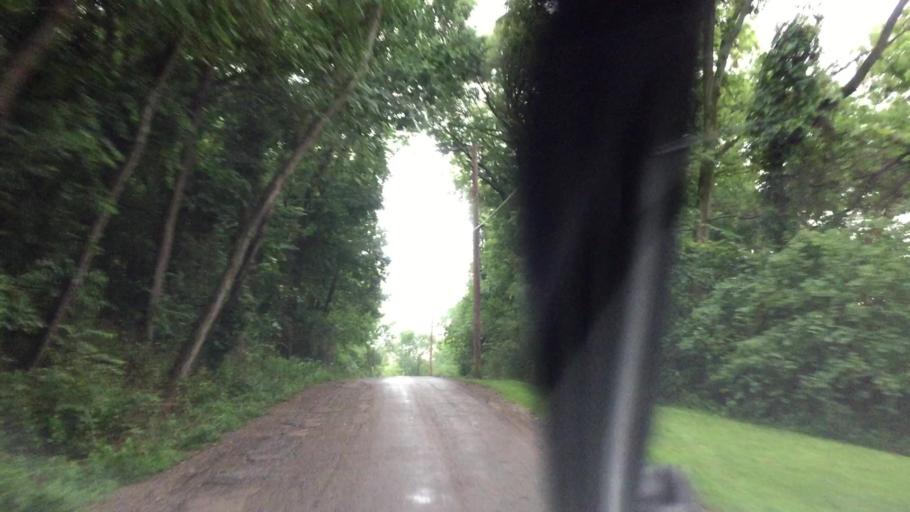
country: US
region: Illinois
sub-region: Hancock County
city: Nauvoo
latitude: 40.5352
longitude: -91.3760
